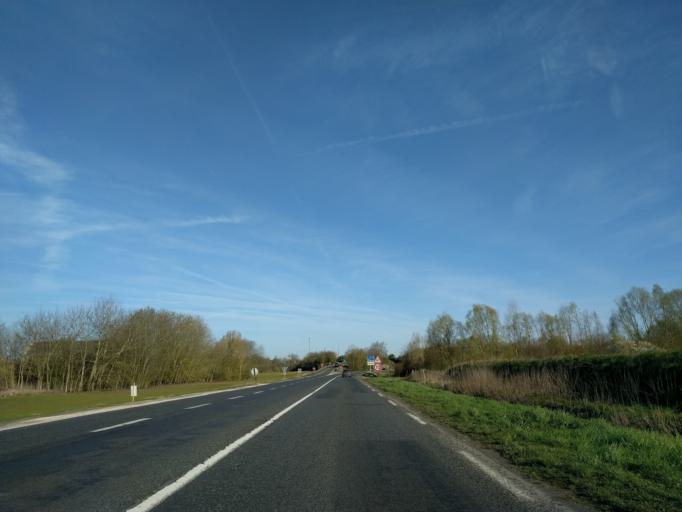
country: FR
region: Ile-de-France
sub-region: Departement de Seine-et-Marne
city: Moissy-Cramayel
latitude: 48.6051
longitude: 2.5833
